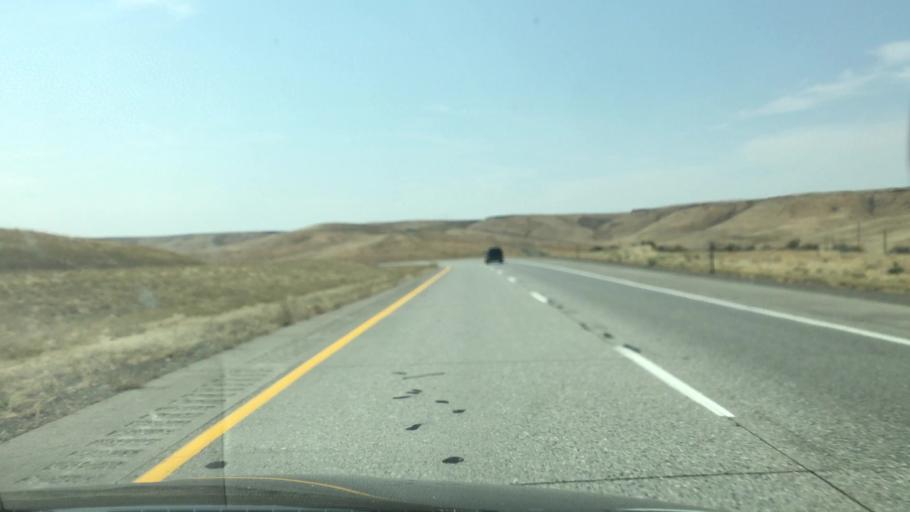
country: US
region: Idaho
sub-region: Elmore County
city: Glenns Ferry
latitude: 42.9644
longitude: -115.3274
